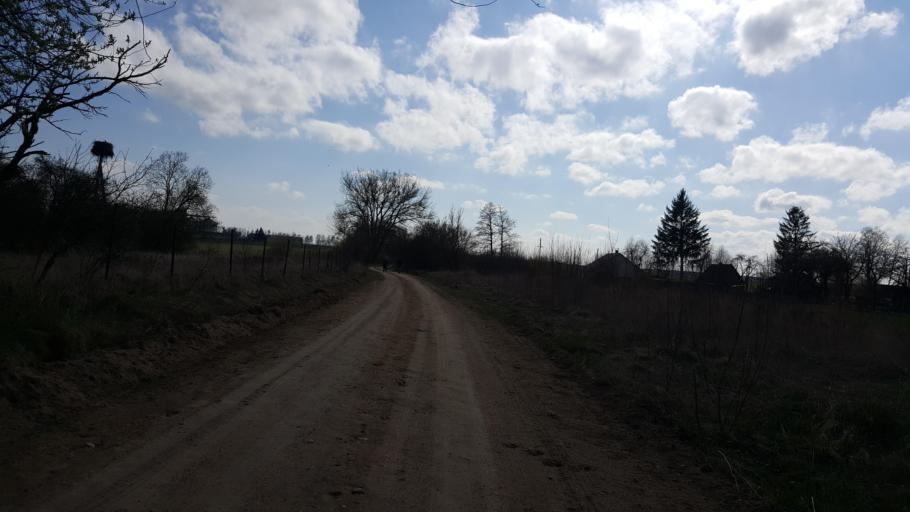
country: BY
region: Brest
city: Kamyanyets
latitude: 52.4071
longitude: 23.7829
